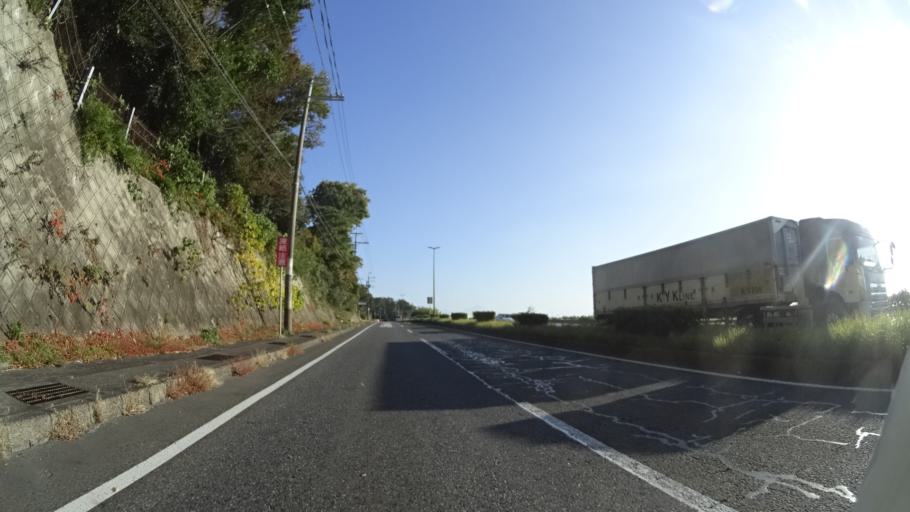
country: JP
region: Shiga Prefecture
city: Kitahama
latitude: 35.2913
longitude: 136.0154
